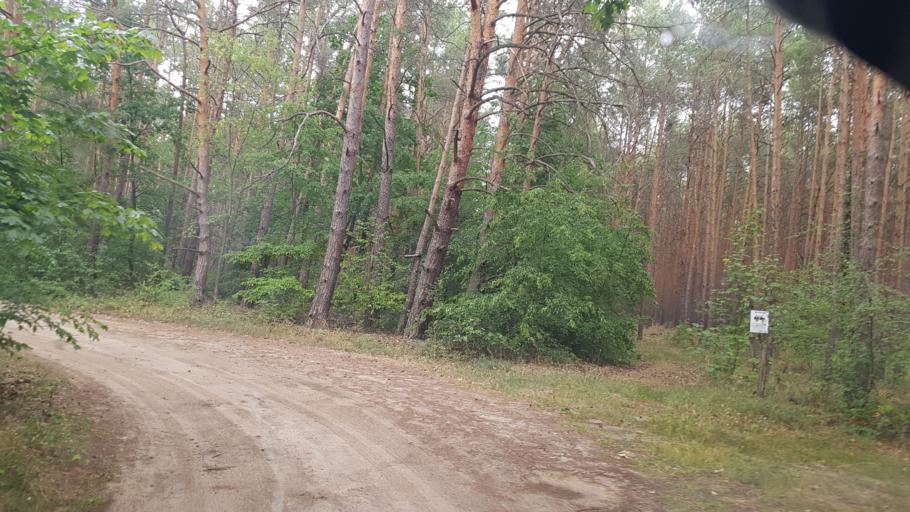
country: DE
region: Brandenburg
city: Schwerin
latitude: 52.1393
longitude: 13.6317
